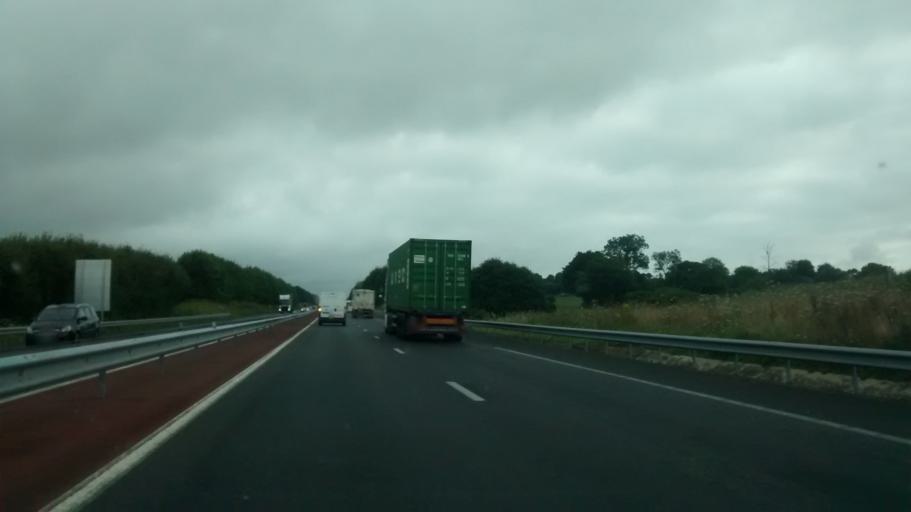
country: FR
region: Lower Normandy
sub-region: Departement de la Manche
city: Saint-Senier-sous-Avranches
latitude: 48.7566
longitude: -1.2787
